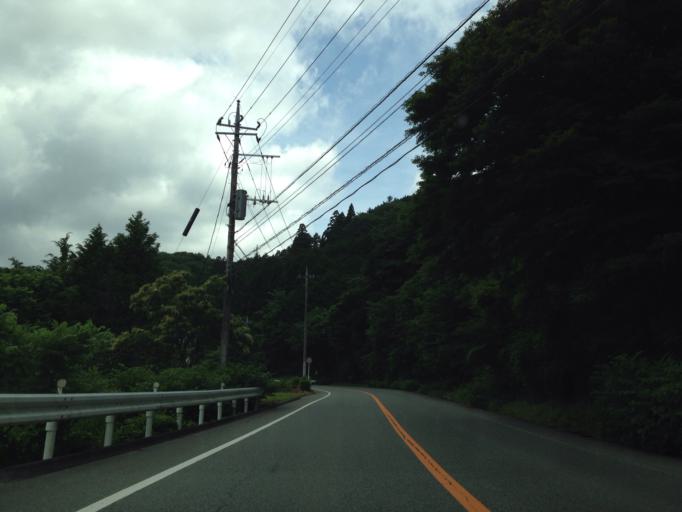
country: JP
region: Shizuoka
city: Heda
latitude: 34.9168
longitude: 138.8757
